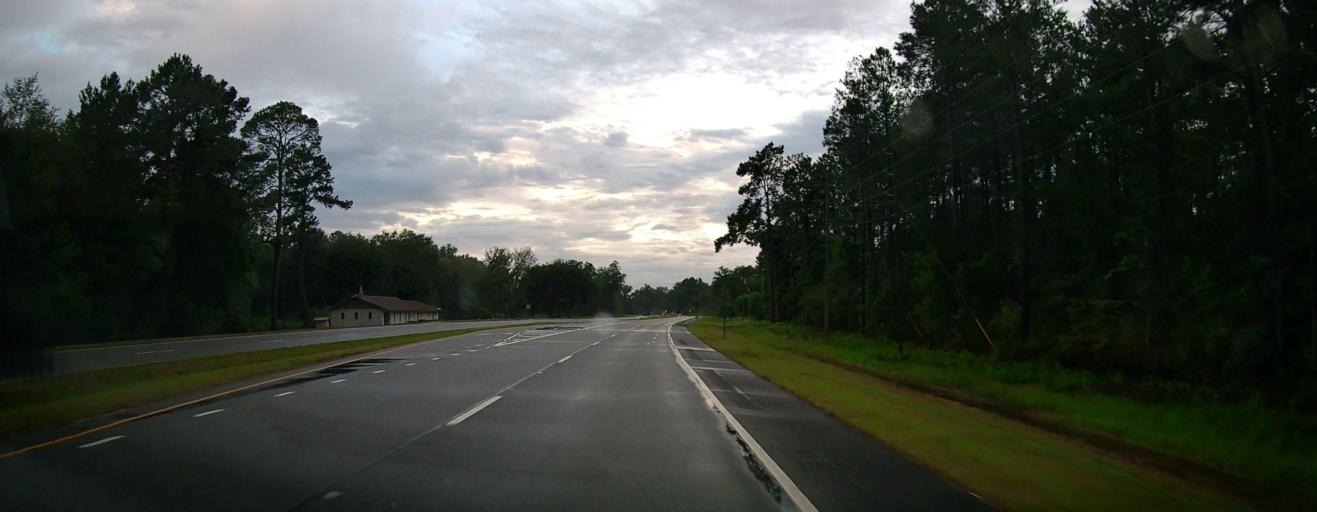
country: US
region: Georgia
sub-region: Lanier County
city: Lakeland
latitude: 30.9417
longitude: -82.9930
